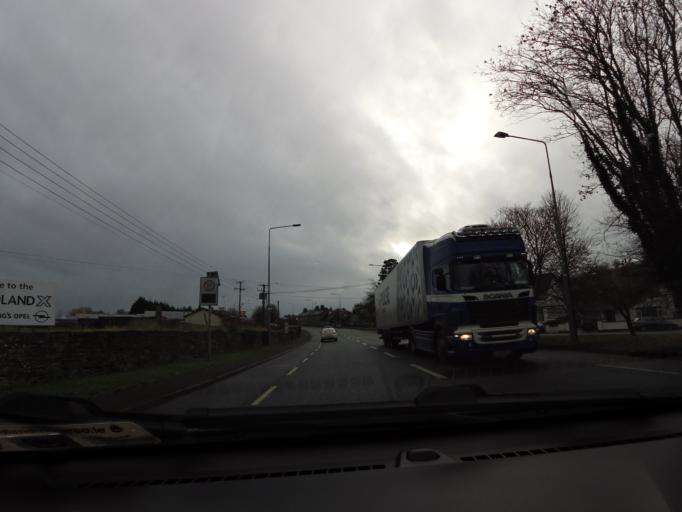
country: IE
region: Munster
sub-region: North Tipperary
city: Roscrea
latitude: 52.9593
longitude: -7.8037
